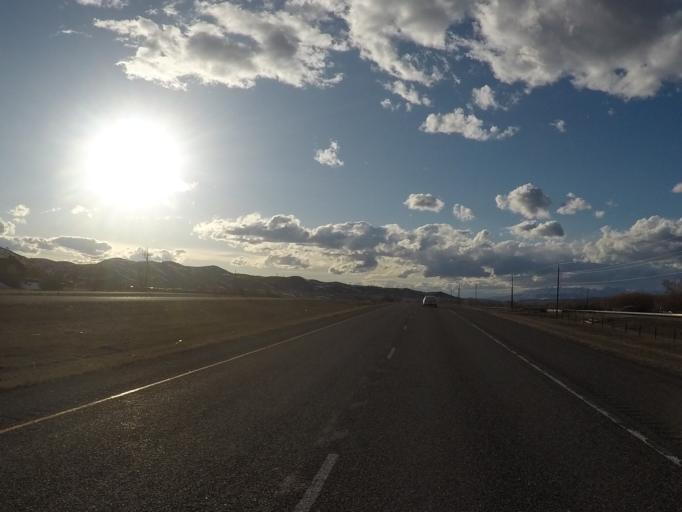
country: US
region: Montana
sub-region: Stillwater County
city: Absarokee
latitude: 45.7083
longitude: -109.6160
